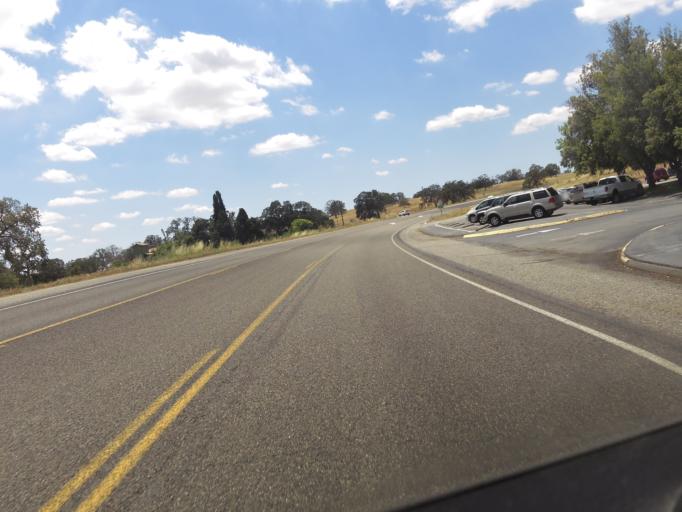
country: US
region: California
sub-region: Madera County
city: Yosemite Lakes
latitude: 37.1209
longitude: -119.6997
